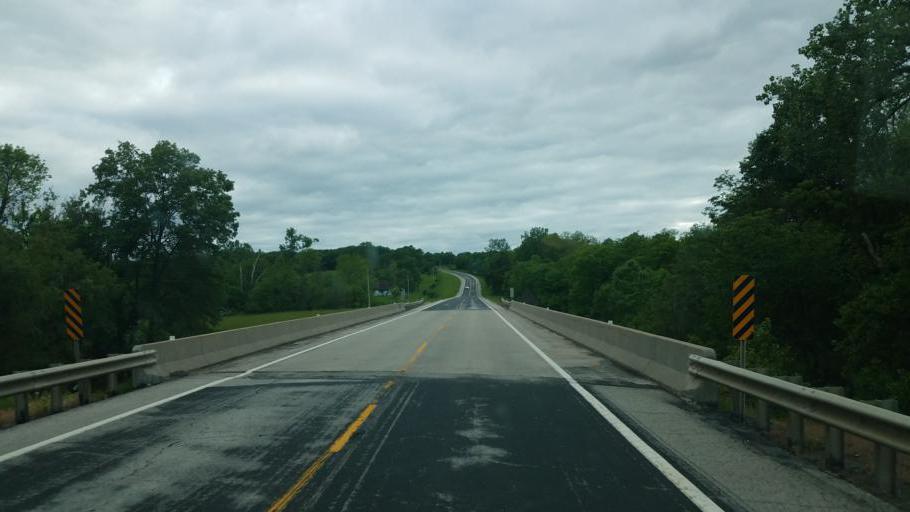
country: US
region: Missouri
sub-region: Mercer County
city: Princeton
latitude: 40.3619
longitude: -93.7375
